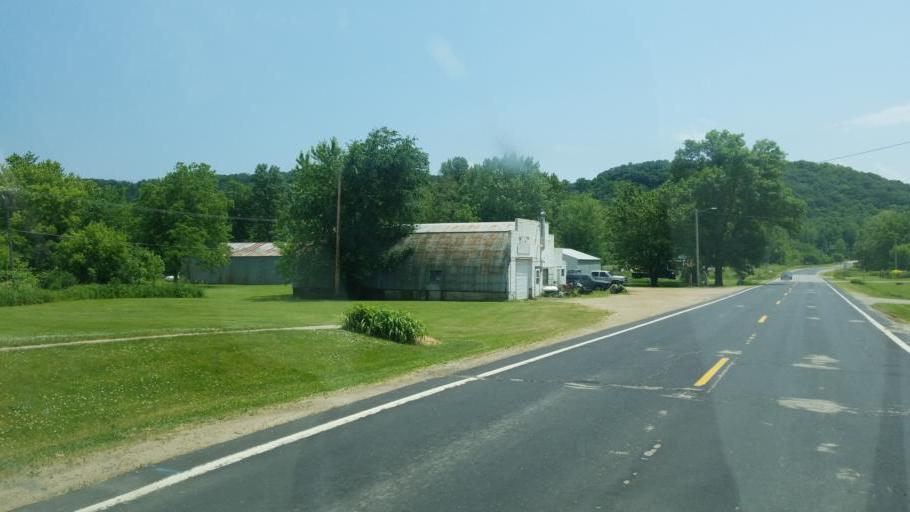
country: US
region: Wisconsin
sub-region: Monroe County
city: Cashton
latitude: 43.5723
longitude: -90.6363
